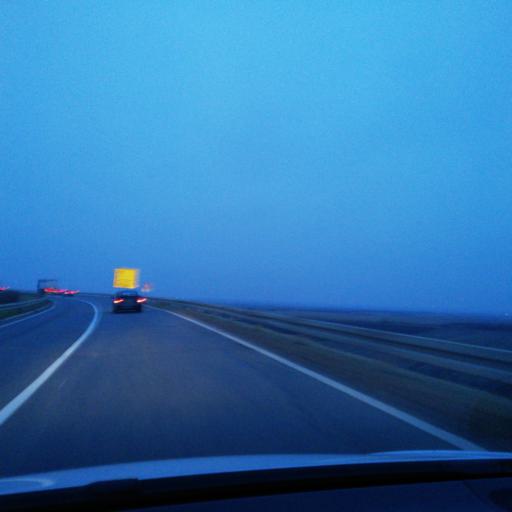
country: RS
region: Autonomna Pokrajina Vojvodina
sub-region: Sremski Okrug
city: Ruma
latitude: 44.9866
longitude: 19.8327
